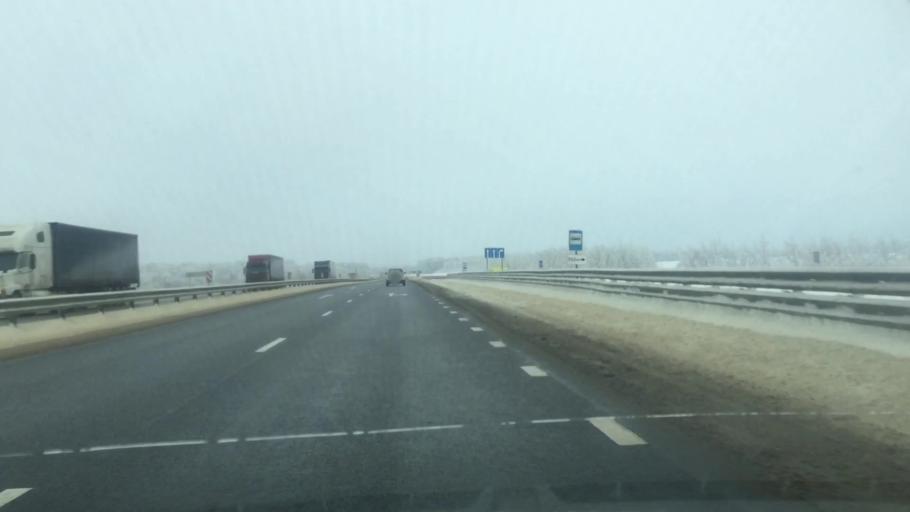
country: RU
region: Lipetsk
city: Zadonsk
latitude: 52.5032
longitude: 38.7554
